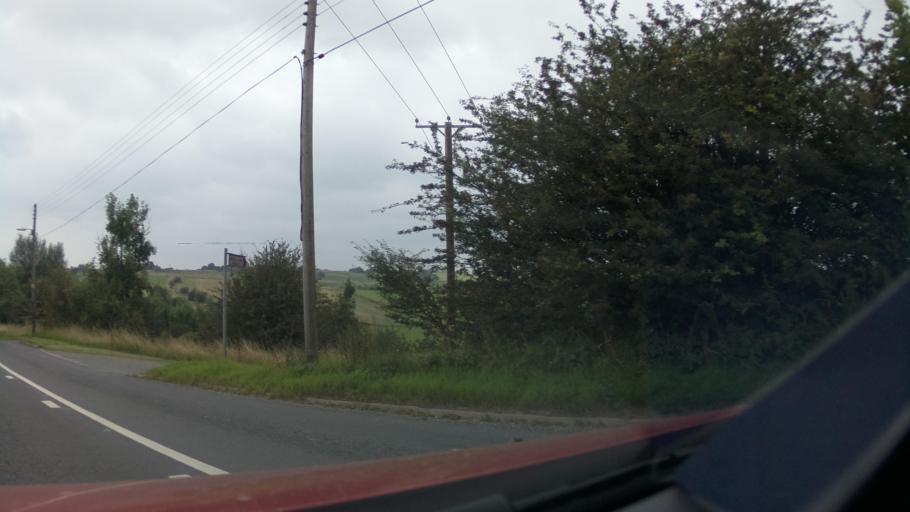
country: GB
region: England
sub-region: Staffordshire
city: Cheadle
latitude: 53.0309
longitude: -1.8909
